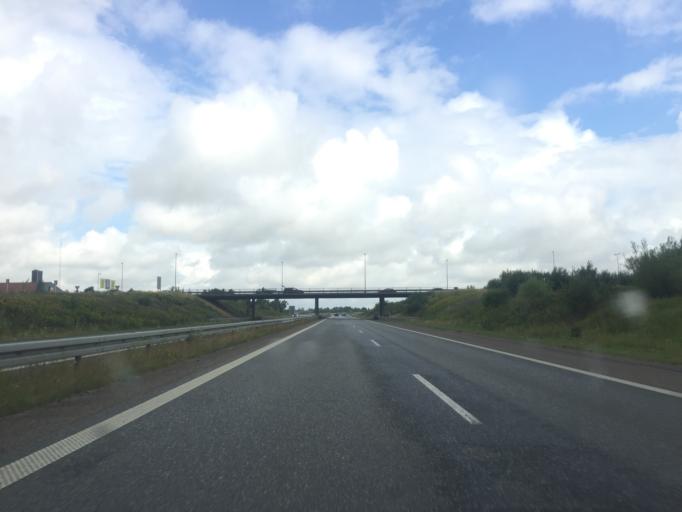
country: DK
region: South Denmark
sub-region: Faaborg-Midtfyn Kommune
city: Ringe
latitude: 55.2355
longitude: 10.4925
